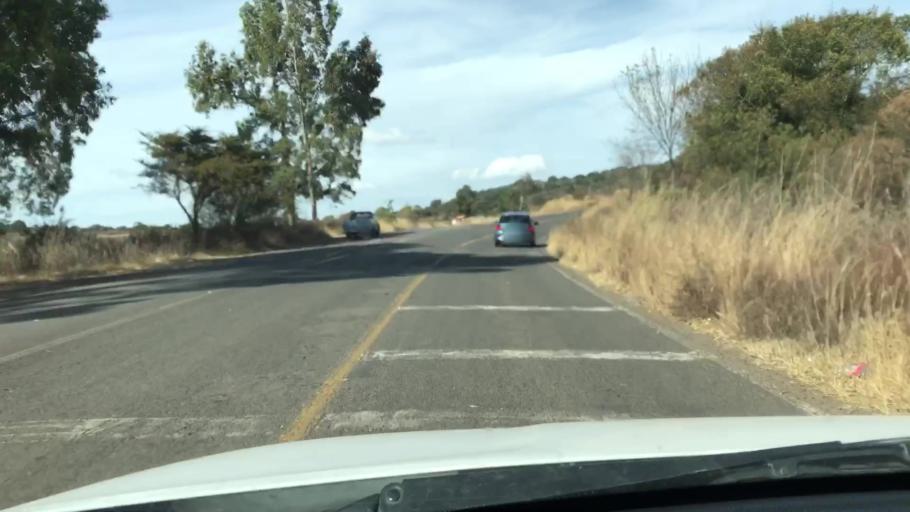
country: MX
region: Jalisco
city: Chiquilistlan
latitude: 20.1869
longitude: -103.7247
